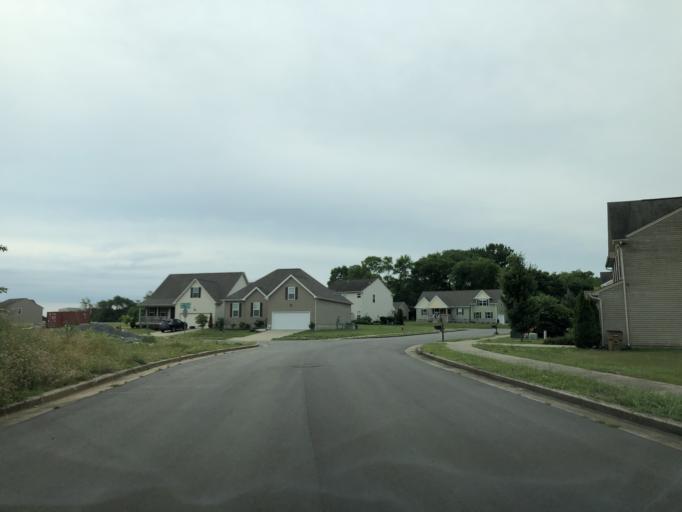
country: US
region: Tennessee
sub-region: Davidson County
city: Goodlettsville
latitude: 36.2809
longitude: -86.6997
